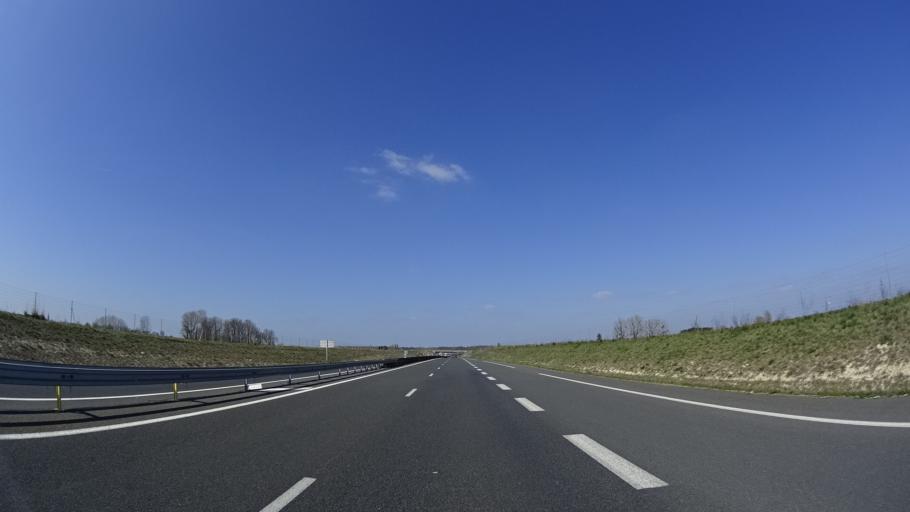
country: FR
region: Pays de la Loire
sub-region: Departement de Maine-et-Loire
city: Saint-Jean
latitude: 47.2874
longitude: -0.3770
